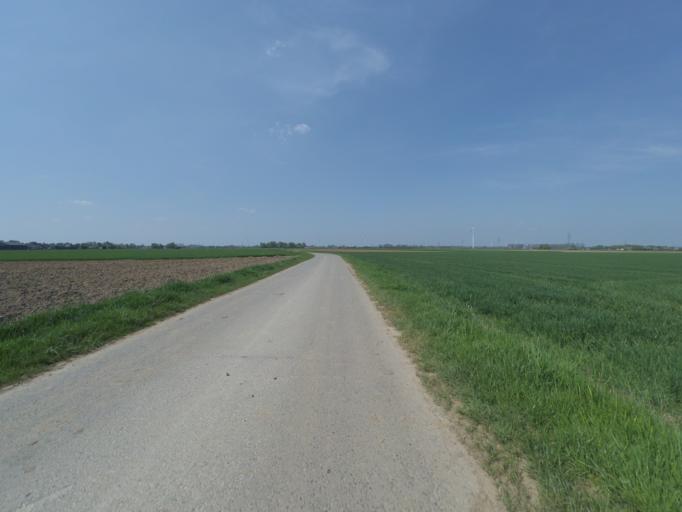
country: NL
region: Gelderland
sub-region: Oude IJsselstreek
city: Gendringen
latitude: 51.8300
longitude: 6.3395
